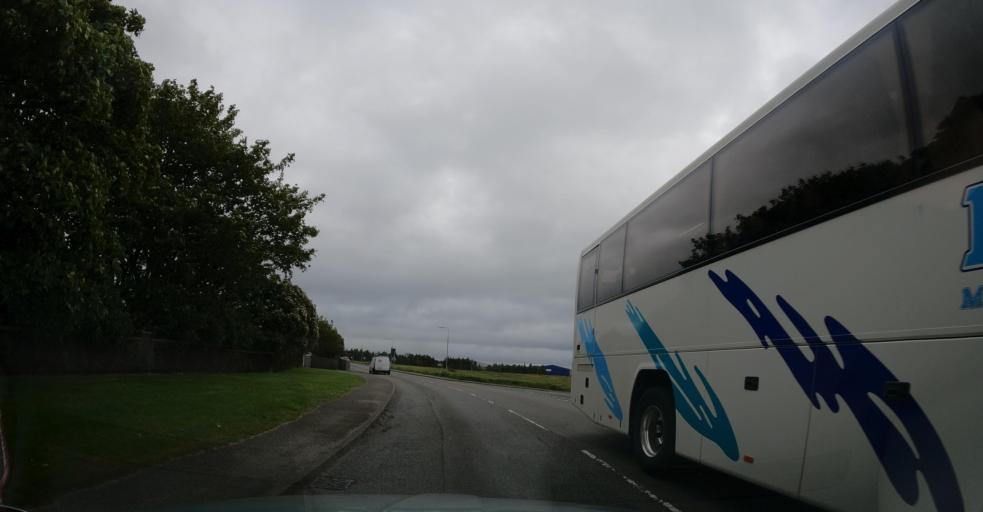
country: GB
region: Scotland
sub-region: Eilean Siar
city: Stornoway
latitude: 58.2035
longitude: -6.3506
